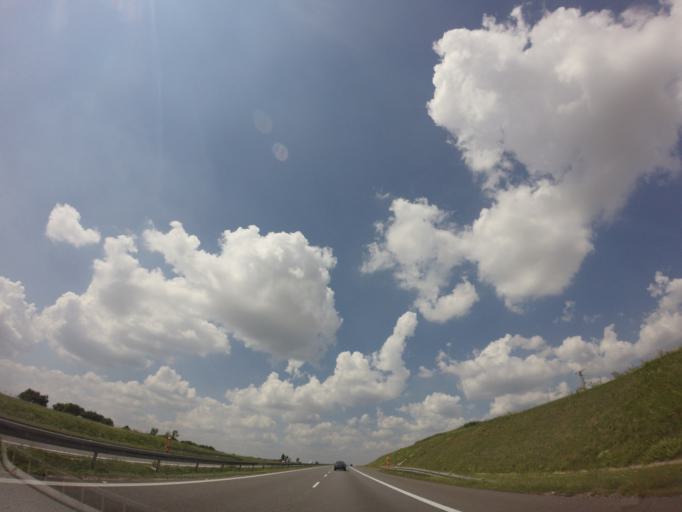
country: PL
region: Opole Voivodeship
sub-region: Powiat strzelecki
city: Lesnica
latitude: 50.4612
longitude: 18.2305
